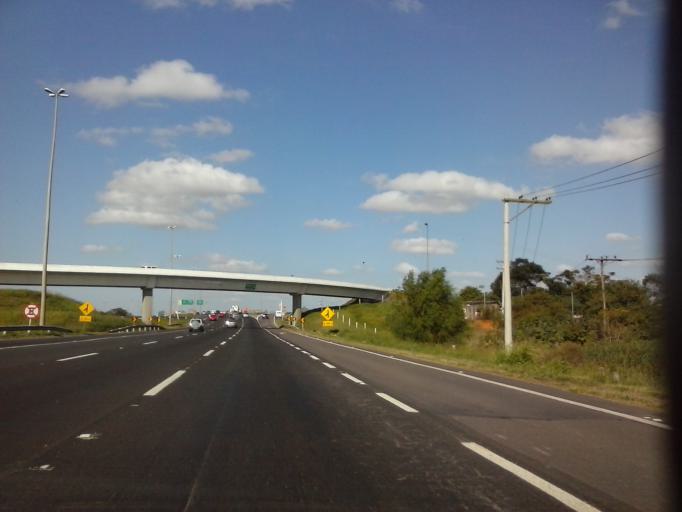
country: BR
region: Rio Grande do Sul
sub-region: Canoas
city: Canoas
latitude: -29.9713
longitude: -51.1825
